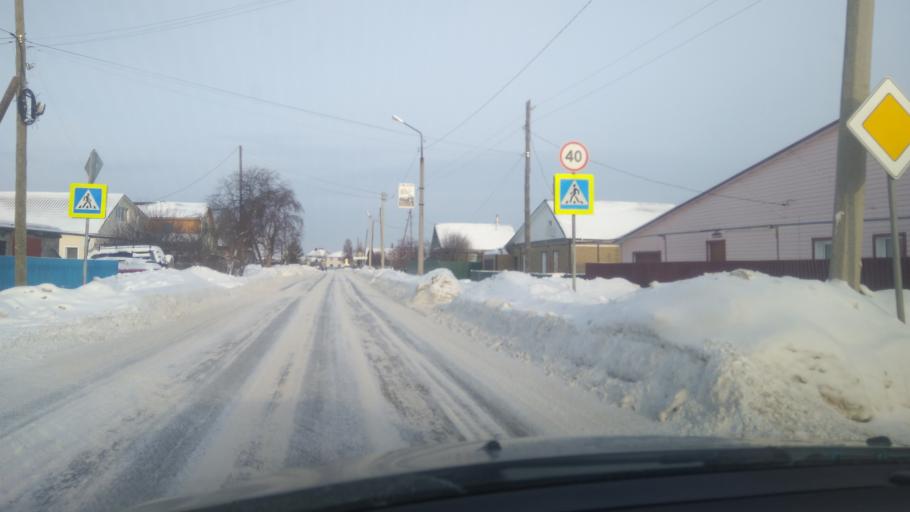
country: RU
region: Sverdlovsk
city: Sukhoy Log
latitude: 56.9047
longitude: 62.0237
